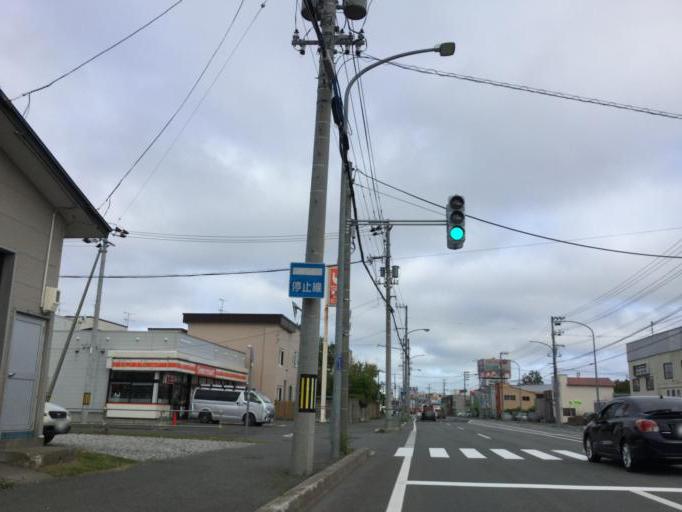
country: JP
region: Hokkaido
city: Wakkanai
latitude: 45.4021
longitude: 141.6790
